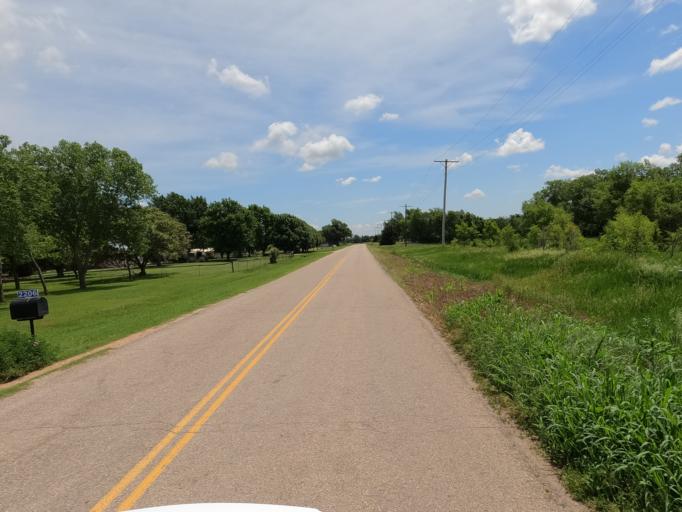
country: US
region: Kansas
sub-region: Reno County
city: South Hutchinson
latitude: 37.9334
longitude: -97.8893
